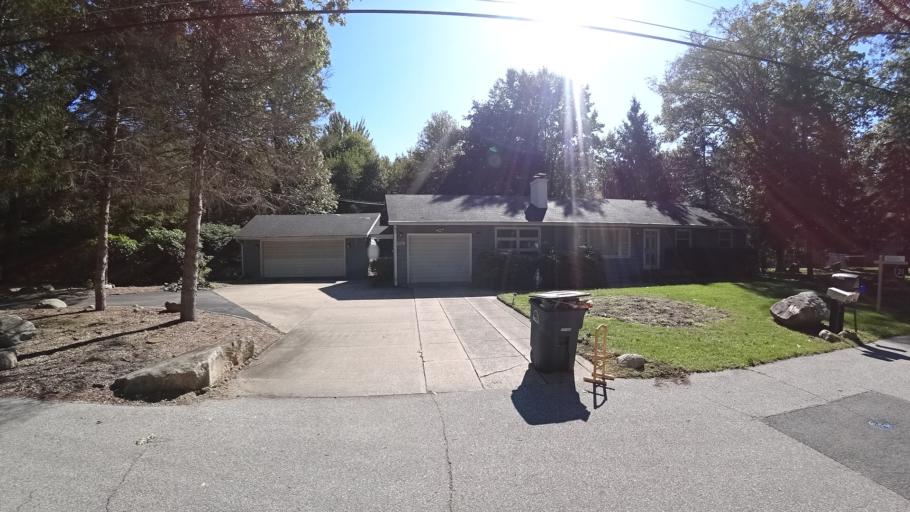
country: US
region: Indiana
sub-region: LaPorte County
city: Long Beach
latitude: 41.7494
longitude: -86.8328
